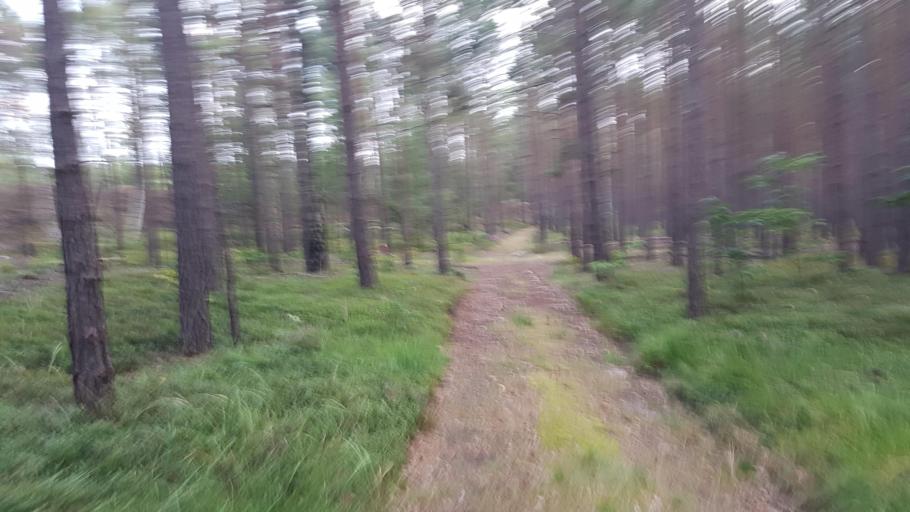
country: DE
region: Brandenburg
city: Trobitz
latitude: 51.6114
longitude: 13.4406
